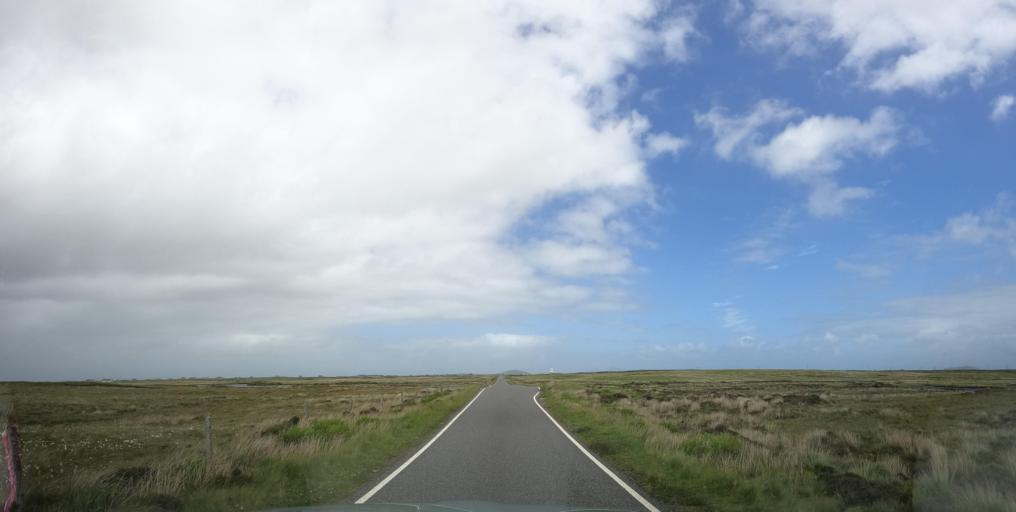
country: GB
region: Scotland
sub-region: Eilean Siar
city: Benbecula
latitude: 57.3767
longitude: -7.3444
